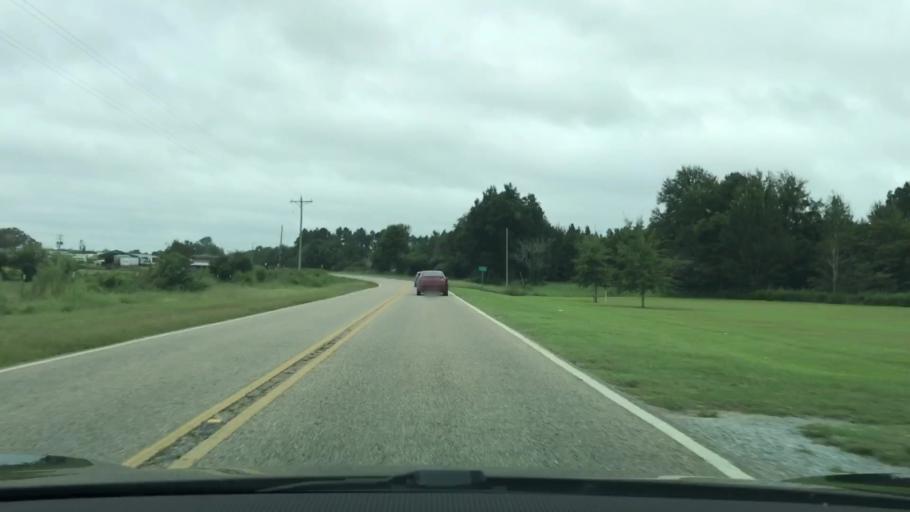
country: US
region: Alabama
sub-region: Geneva County
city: Samson
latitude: 31.1803
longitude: -86.1463
